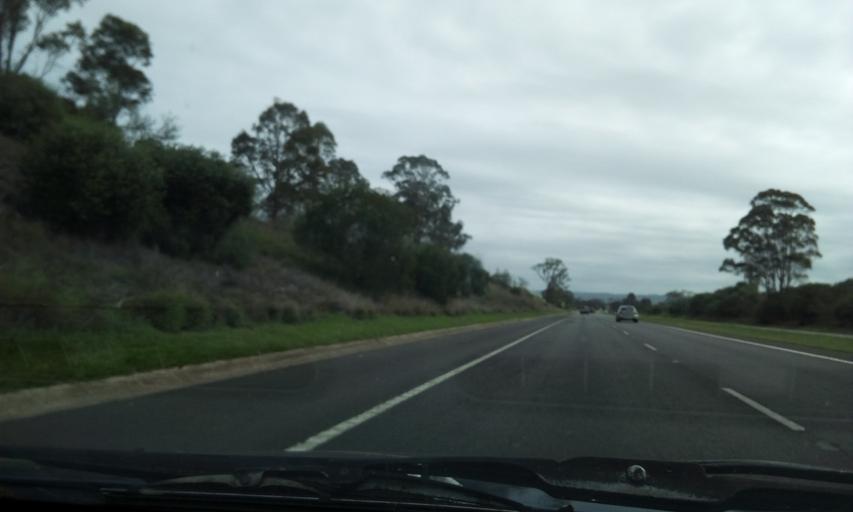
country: AU
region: New South Wales
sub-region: Camden
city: Narellan Vale
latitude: -34.0575
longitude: 150.7320
